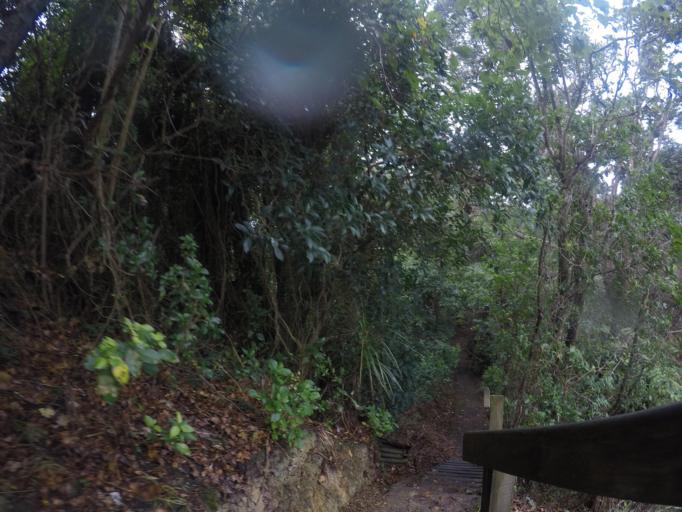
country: NZ
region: Auckland
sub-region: Auckland
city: North Shore
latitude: -36.7795
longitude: 174.6981
